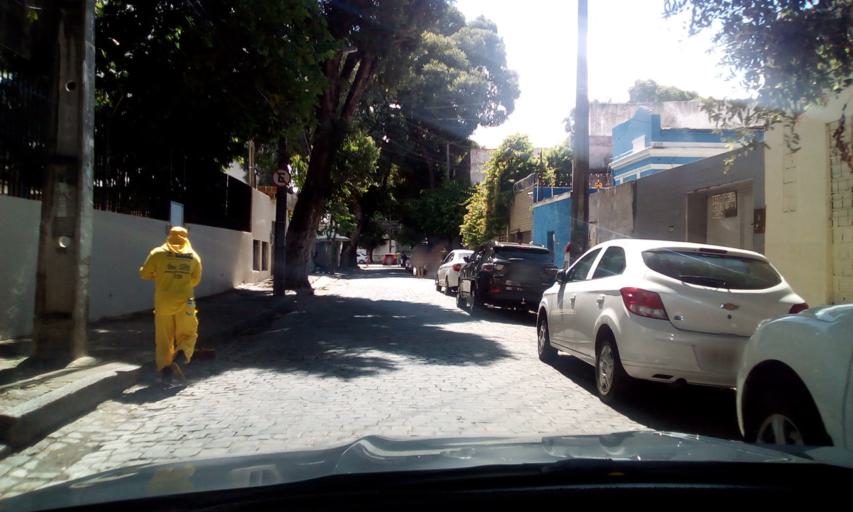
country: BR
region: Pernambuco
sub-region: Recife
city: Recife
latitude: -8.0522
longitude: -34.8889
